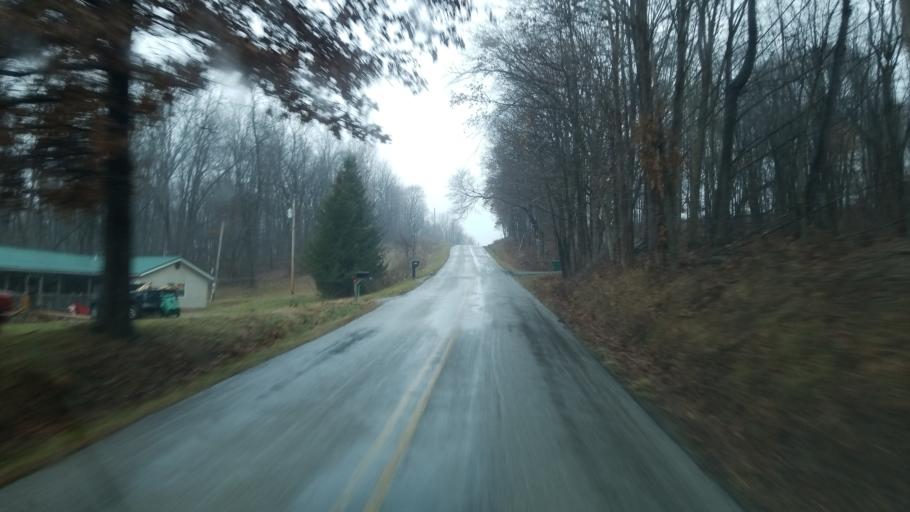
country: US
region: Ohio
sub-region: Licking County
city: Utica
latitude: 40.2191
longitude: -82.3369
